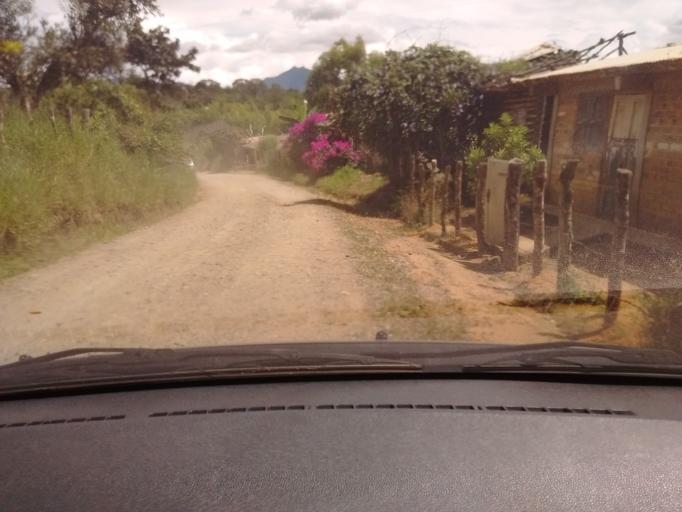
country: CO
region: Cauca
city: El Tambo
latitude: 2.4535
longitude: -76.8257
